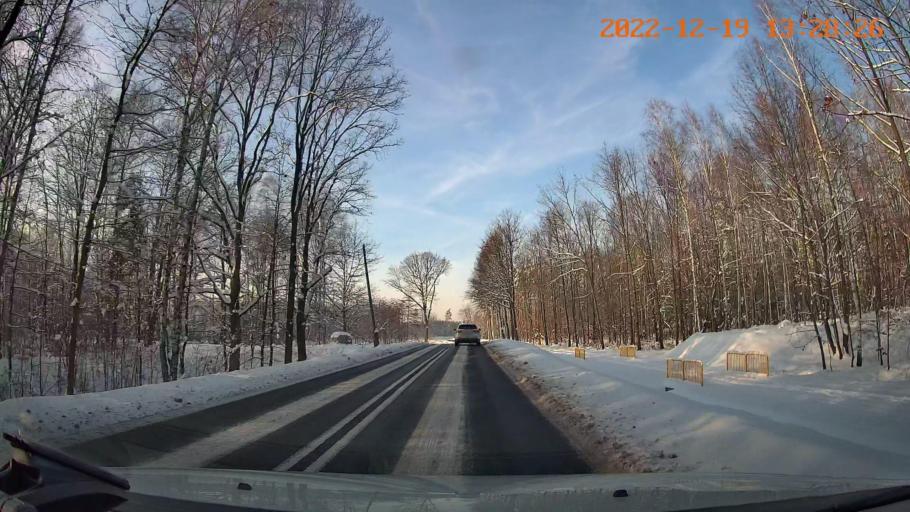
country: PL
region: Silesian Voivodeship
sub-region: Powiat bierunsko-ledzinski
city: Ledziny
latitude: 50.1118
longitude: 19.1281
